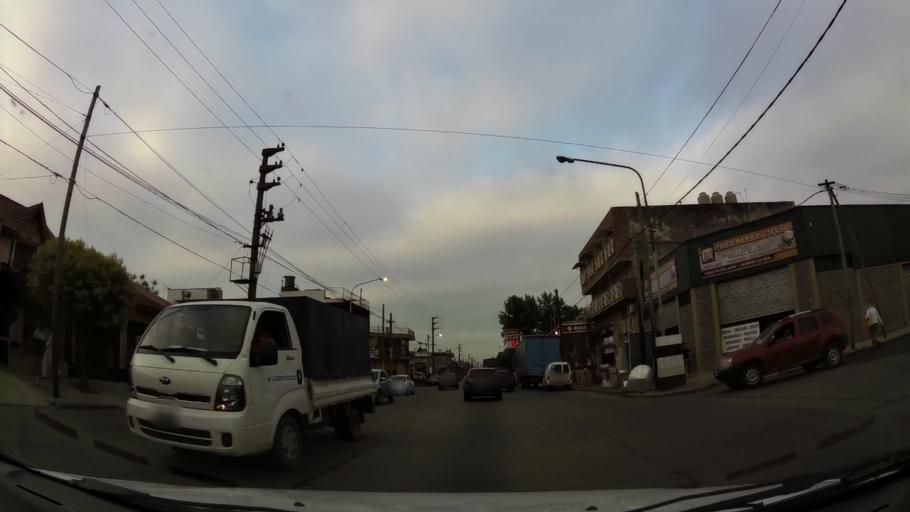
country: AR
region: Buenos Aires
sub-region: Partido de Moron
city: Moron
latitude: -34.6706
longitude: -58.6054
